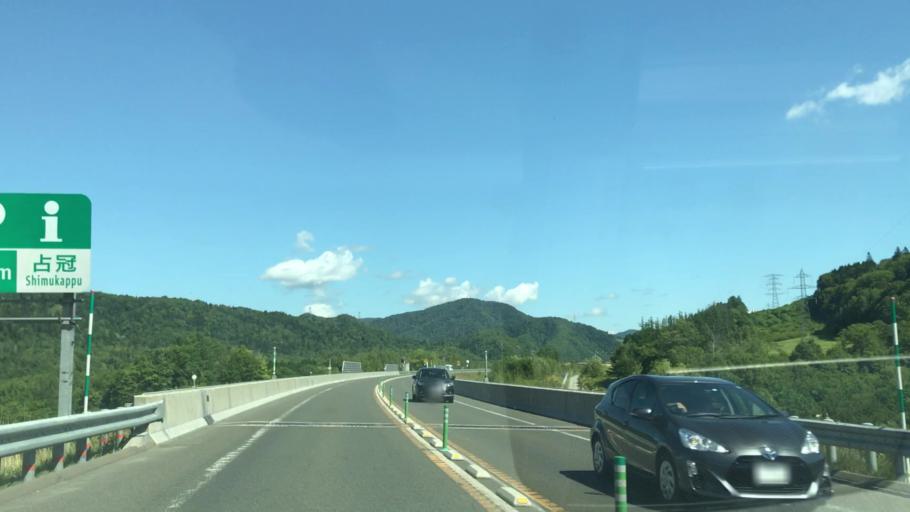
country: JP
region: Hokkaido
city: Shimo-furano
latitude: 43.0017
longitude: 142.4114
